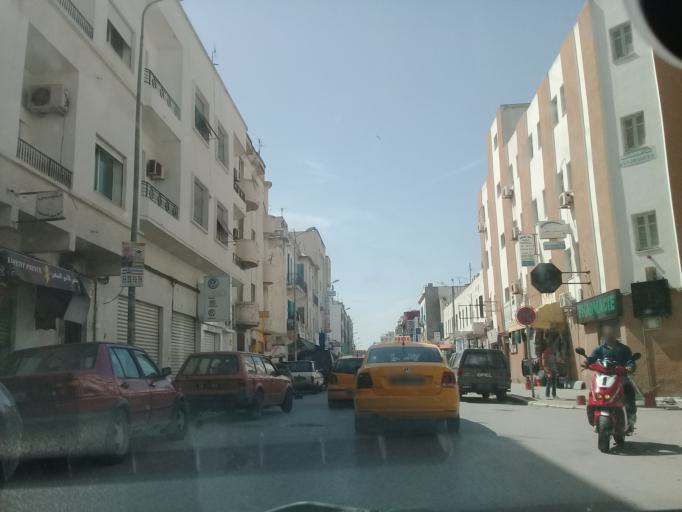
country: TN
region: Tunis
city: Tunis
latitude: 36.8111
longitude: 10.1770
